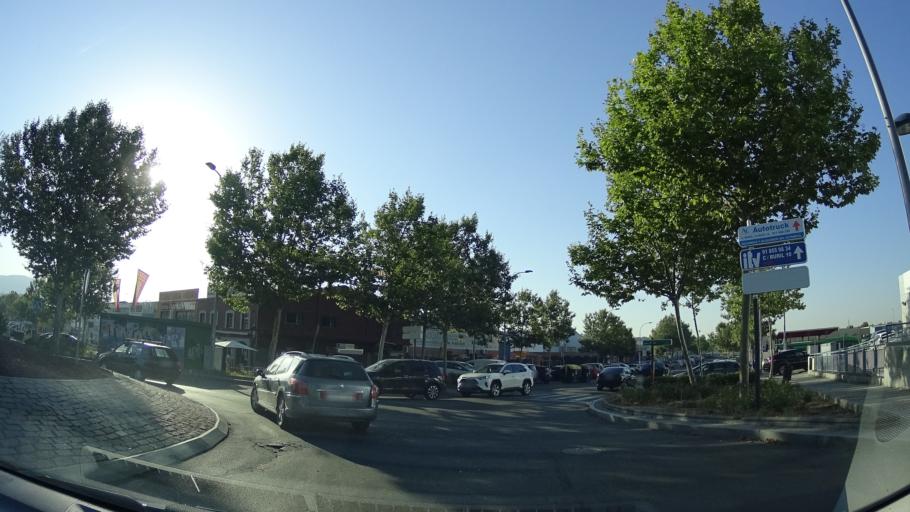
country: ES
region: Madrid
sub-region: Provincia de Madrid
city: Collado-Villalba
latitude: 40.6260
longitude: -4.0223
